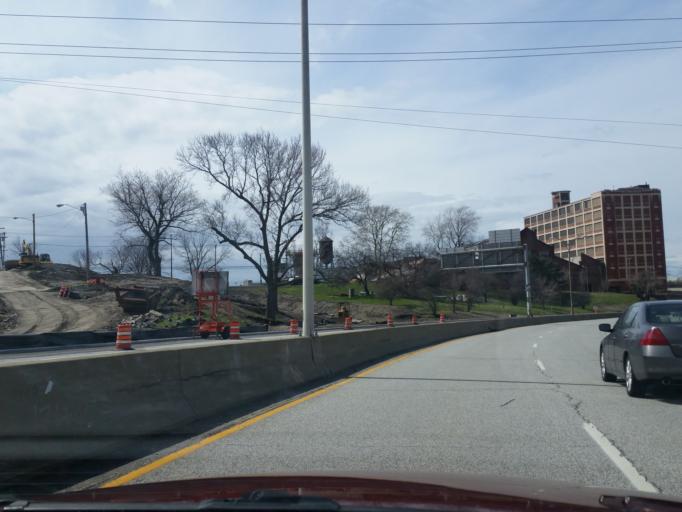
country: US
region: Ohio
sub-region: Cuyahoga County
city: Cleveland
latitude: 41.4894
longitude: -81.7237
